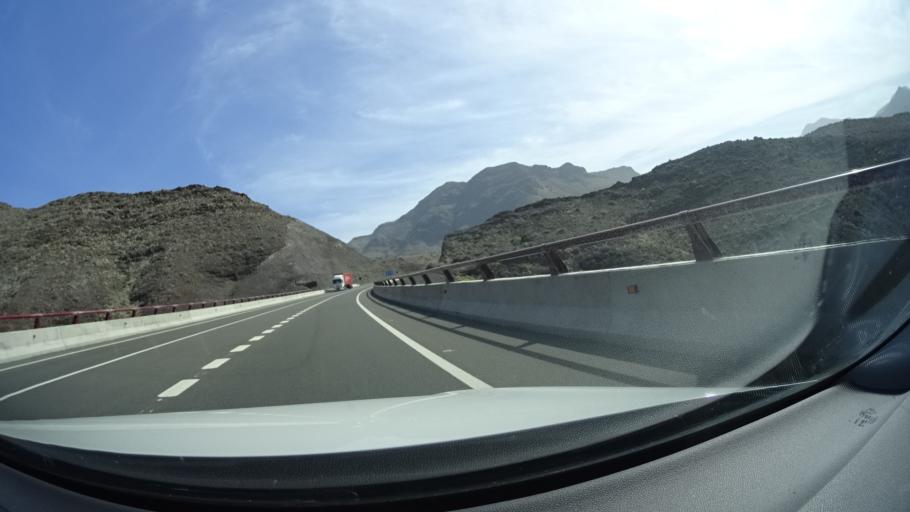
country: ES
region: Canary Islands
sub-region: Provincia de Las Palmas
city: San Nicolas
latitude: 28.0119
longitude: -15.7814
